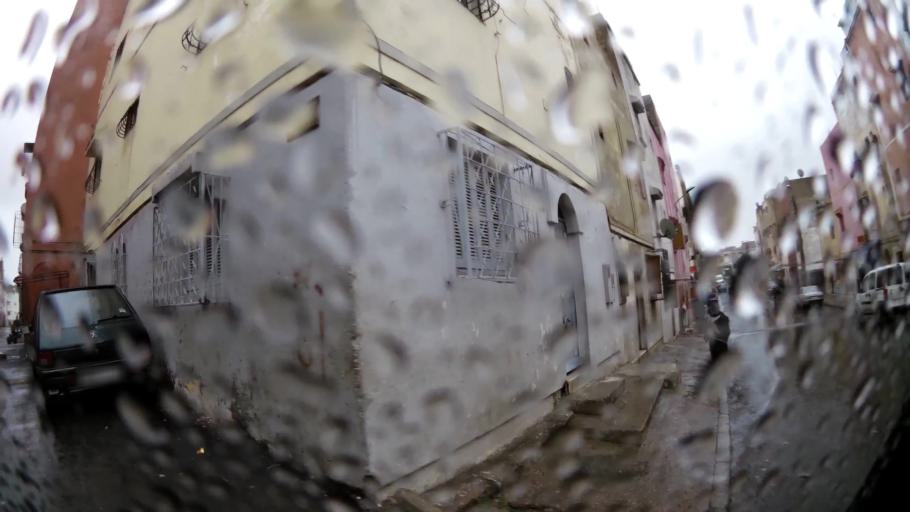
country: MA
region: Grand Casablanca
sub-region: Mediouna
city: Tit Mellil
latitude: 33.5700
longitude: -7.5314
